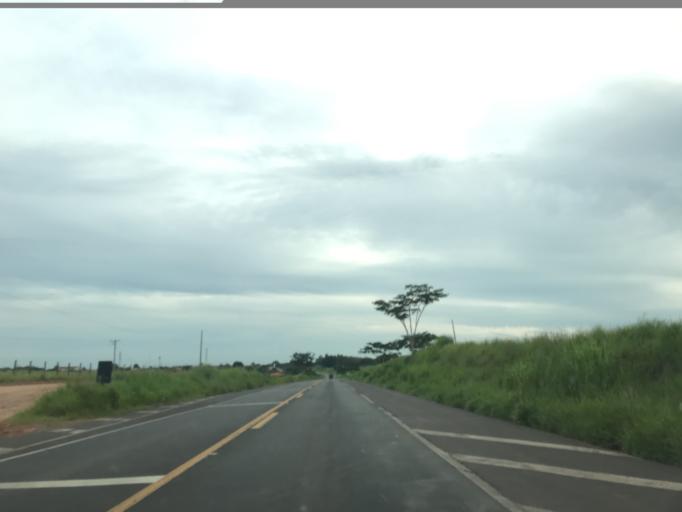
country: BR
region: Sao Paulo
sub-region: Tupa
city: Tupa
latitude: -21.6452
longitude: -50.5075
